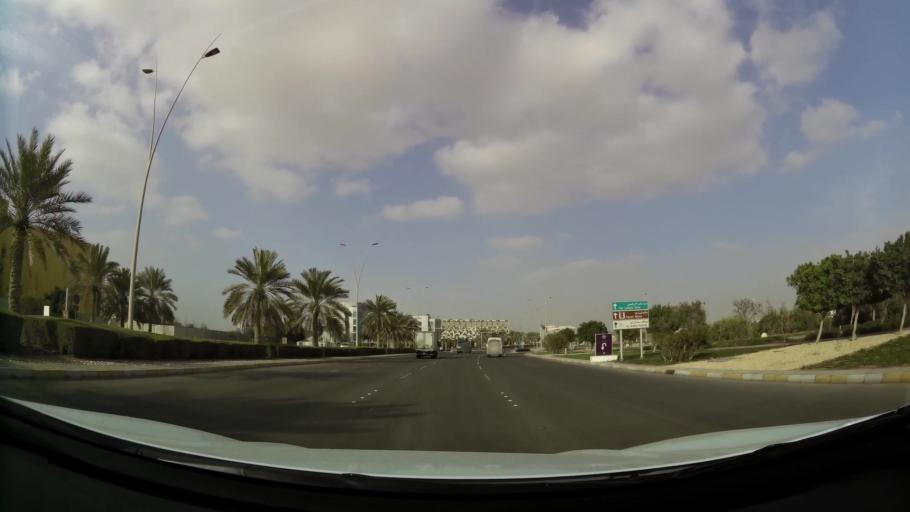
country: AE
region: Abu Dhabi
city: Abu Dhabi
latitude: 24.4908
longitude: 54.6028
